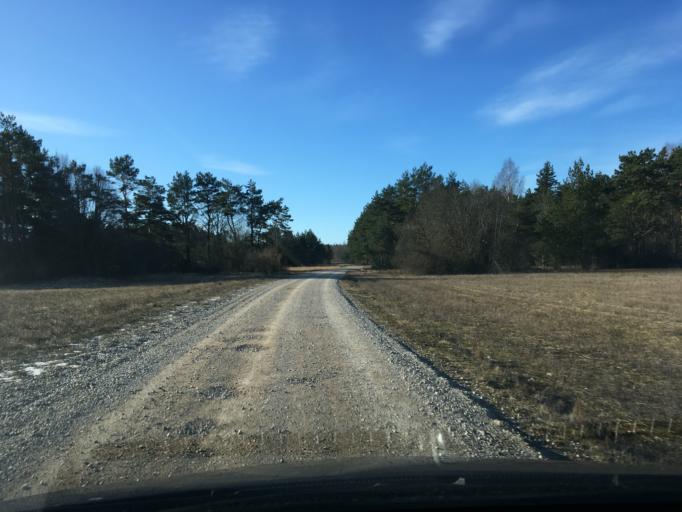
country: EE
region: Laeaene
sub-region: Lihula vald
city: Lihula
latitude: 58.5758
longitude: 23.6993
